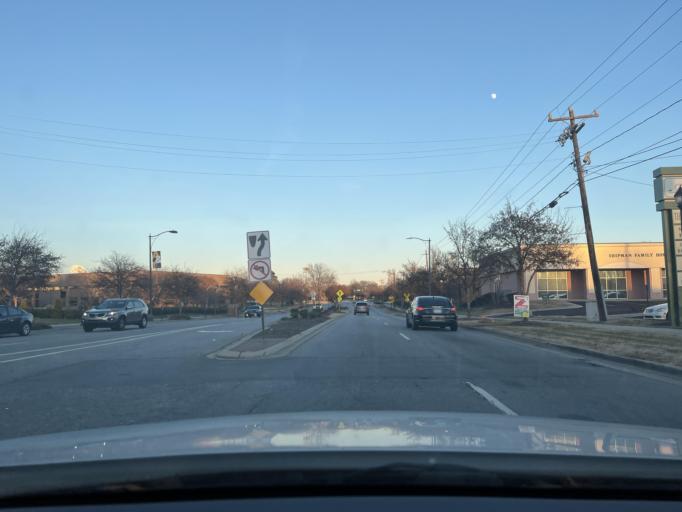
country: US
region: North Carolina
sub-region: Guilford County
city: Greensboro
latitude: 36.0721
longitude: -79.7727
